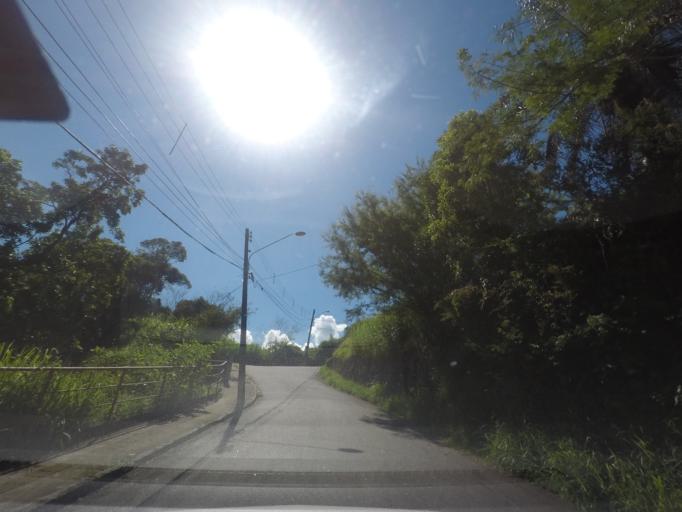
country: BR
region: Rio de Janeiro
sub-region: Petropolis
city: Petropolis
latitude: -22.5104
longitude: -43.1868
